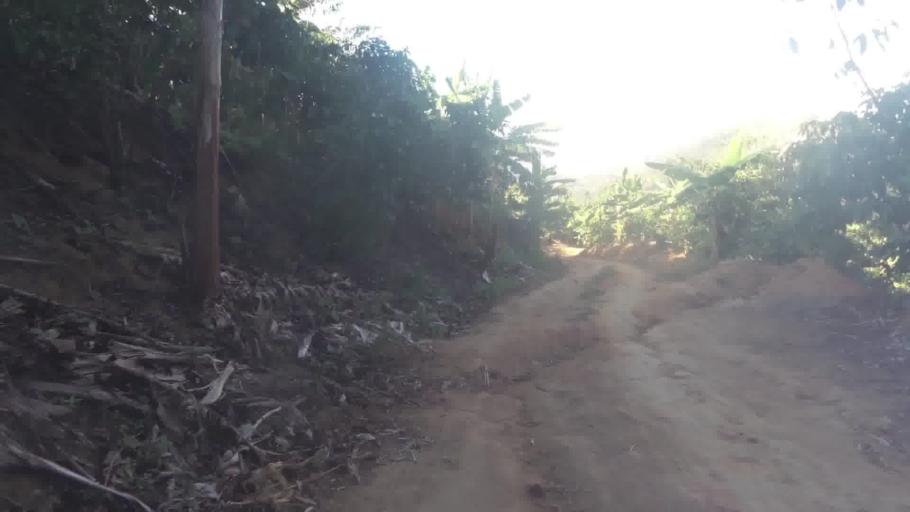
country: BR
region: Espirito Santo
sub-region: Iconha
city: Iconha
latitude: -20.7521
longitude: -40.8073
